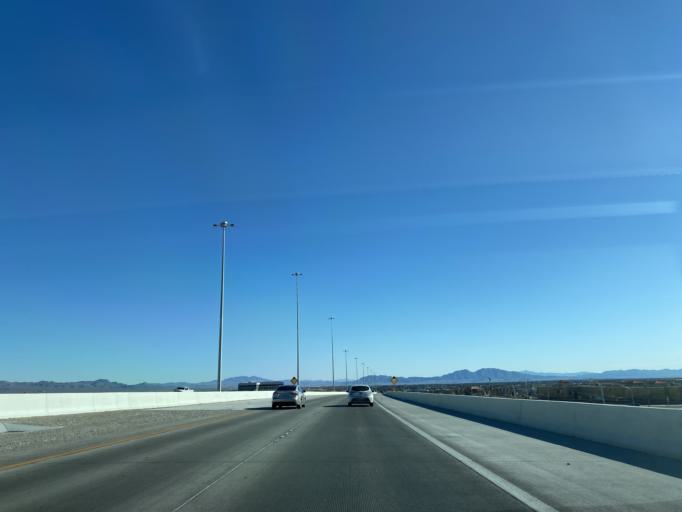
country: US
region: Nevada
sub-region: Clark County
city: Summerlin South
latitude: 36.2799
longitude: -115.2898
